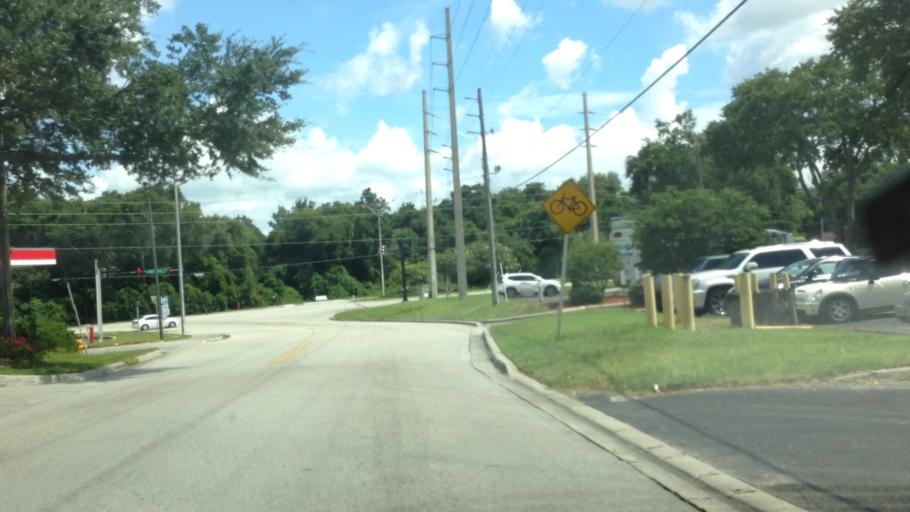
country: US
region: Florida
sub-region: Duval County
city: Jacksonville
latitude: 30.3417
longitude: -81.5373
